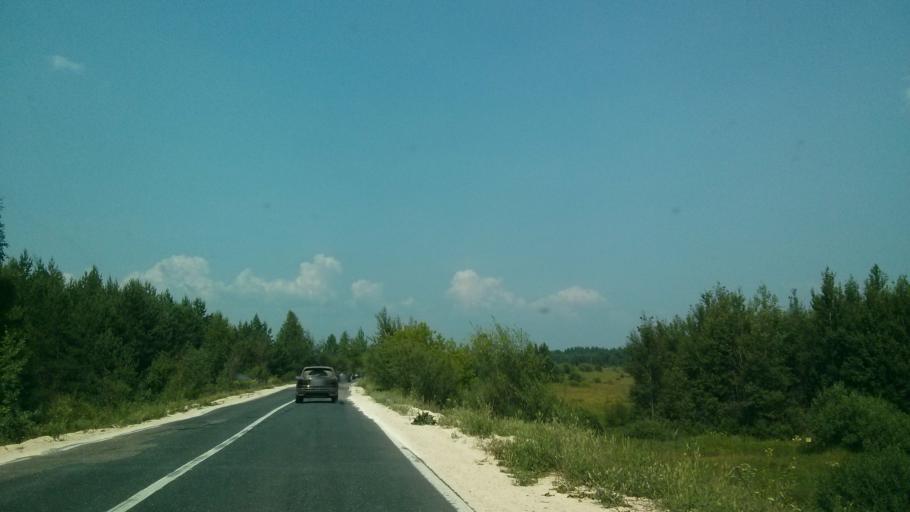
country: RU
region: Nizjnij Novgorod
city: Navashino
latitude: 55.5910
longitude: 42.1518
